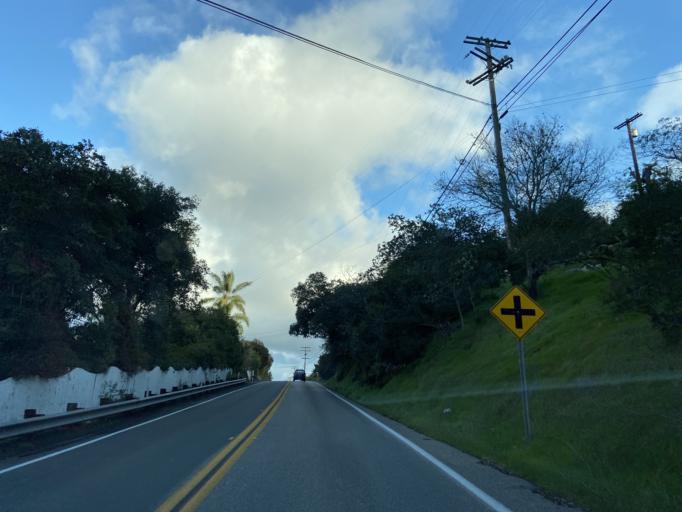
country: US
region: California
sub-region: San Diego County
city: Casa de Oro-Mount Helix
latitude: 32.7752
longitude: -116.9870
